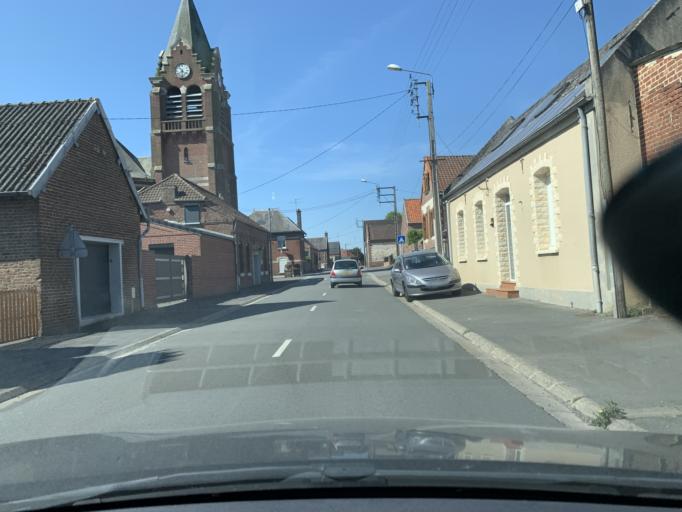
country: FR
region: Nord-Pas-de-Calais
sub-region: Departement du Nord
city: Masnieres
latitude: 50.0958
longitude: 3.2389
